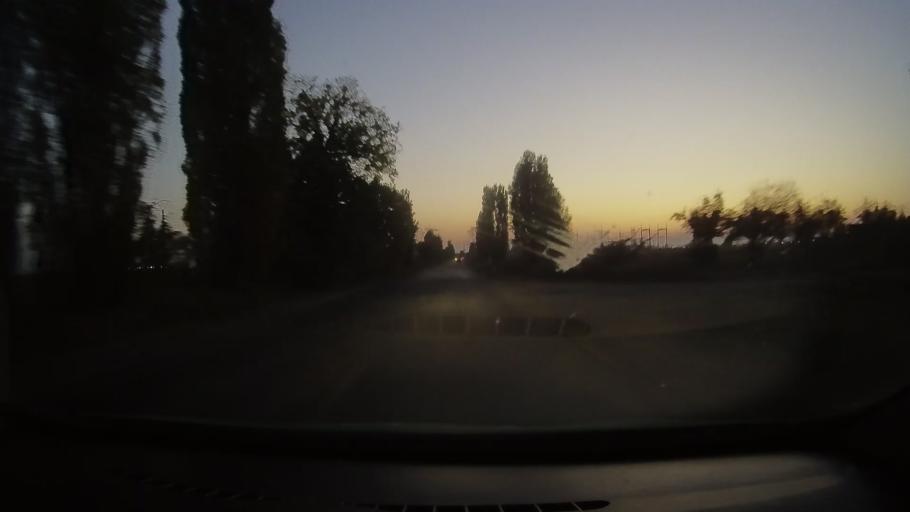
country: RO
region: Arad
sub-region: Comuna Vladimirescu
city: Vladimirescu
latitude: 46.1860
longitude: 21.3859
